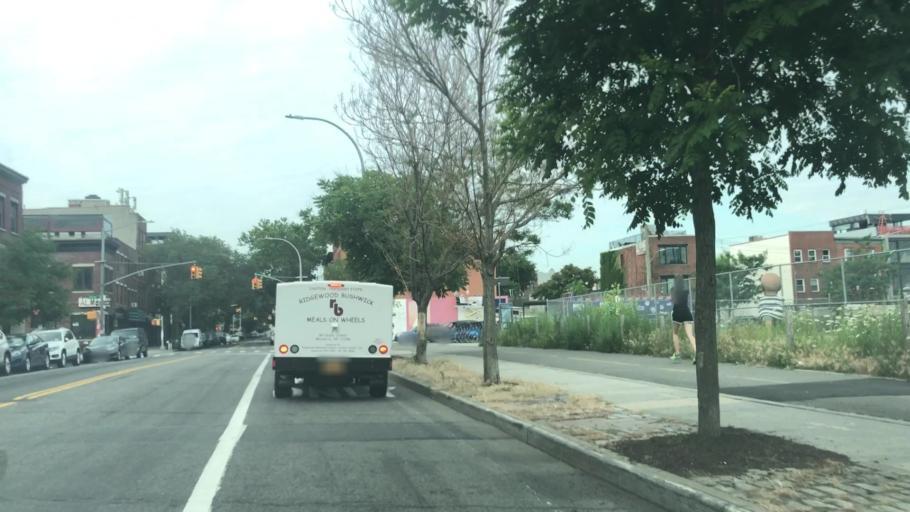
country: US
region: New York
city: New York City
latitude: 40.6863
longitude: -74.0021
